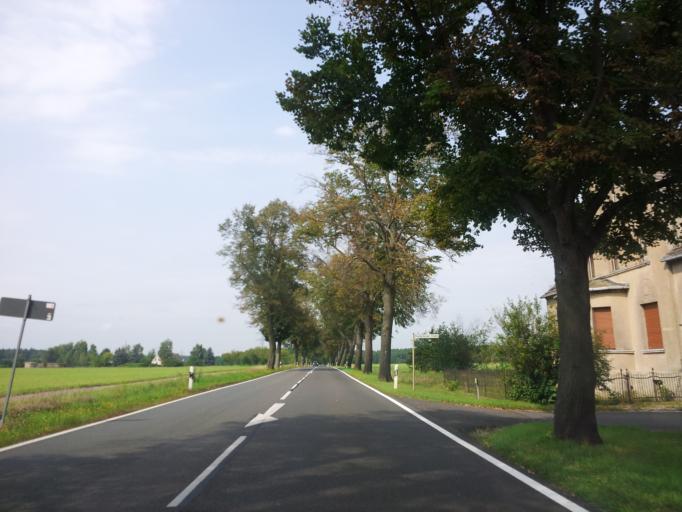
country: DE
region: Brandenburg
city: Niemegk
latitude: 52.0840
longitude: 12.6953
